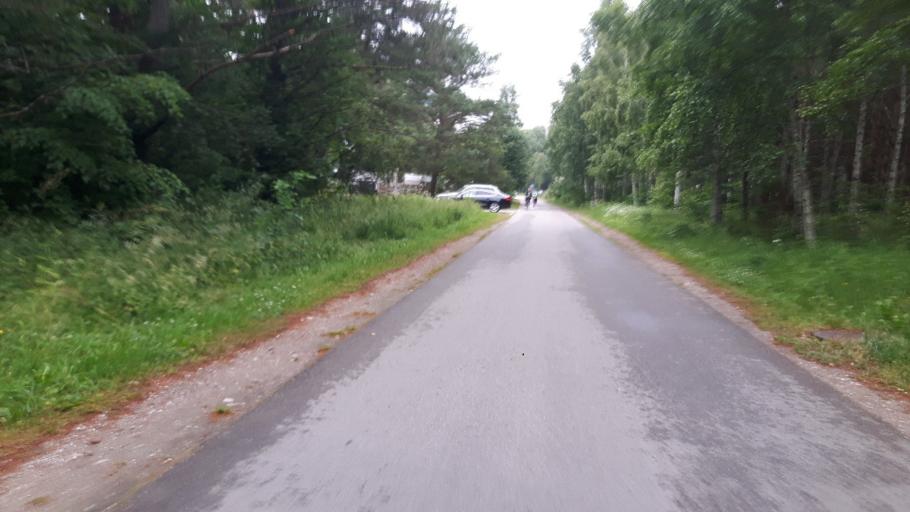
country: LT
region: Klaipedos apskritis
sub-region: Palanga
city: Sventoji
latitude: 56.0016
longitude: 21.0767
